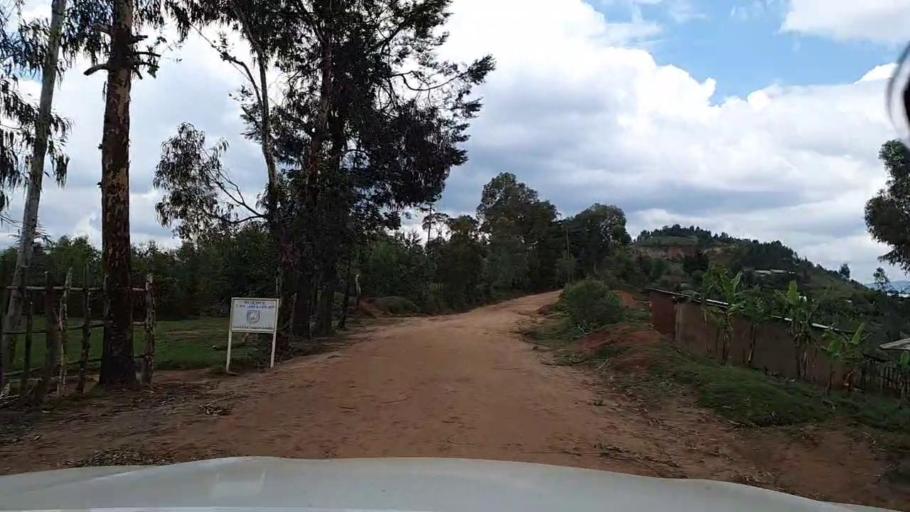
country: RW
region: Southern Province
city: Nzega
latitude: -2.7084
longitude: 29.5159
